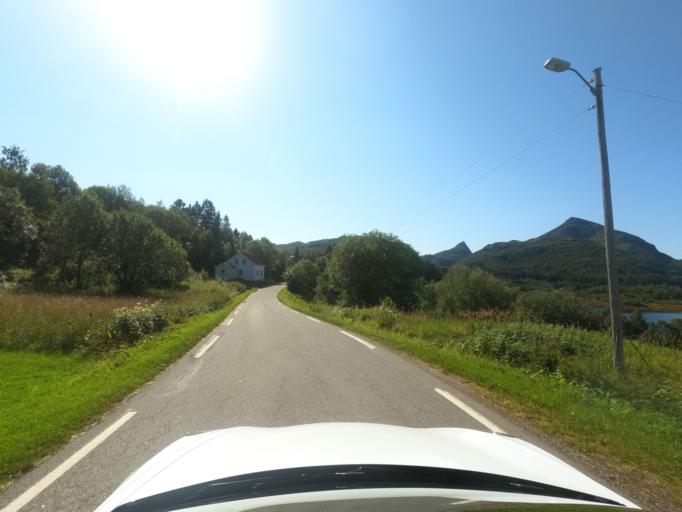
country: NO
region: Nordland
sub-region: Hadsel
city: Stokmarknes
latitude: 68.3059
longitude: 15.0676
